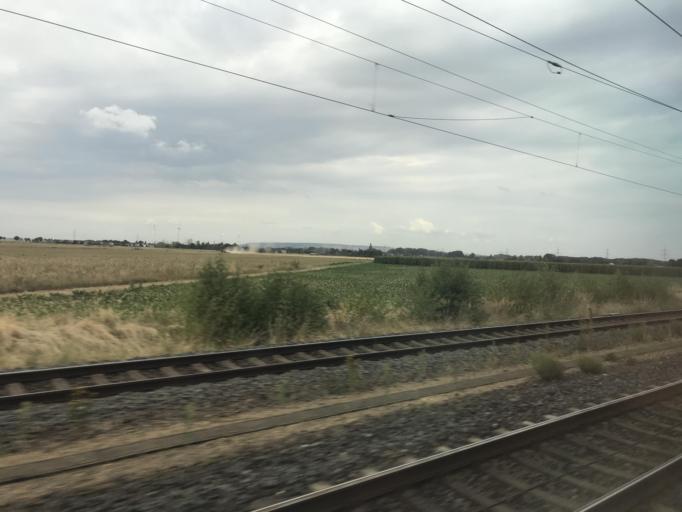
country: DE
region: North Rhine-Westphalia
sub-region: Regierungsbezirk Koln
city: Dueren
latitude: 50.8234
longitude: 6.4983
